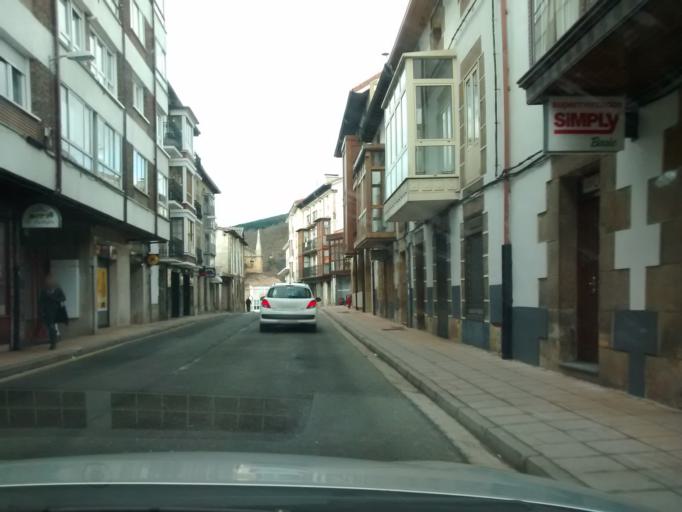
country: ES
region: Castille and Leon
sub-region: Provincia de Burgos
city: Espinosa de los Monteros
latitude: 43.0760
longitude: -3.5505
